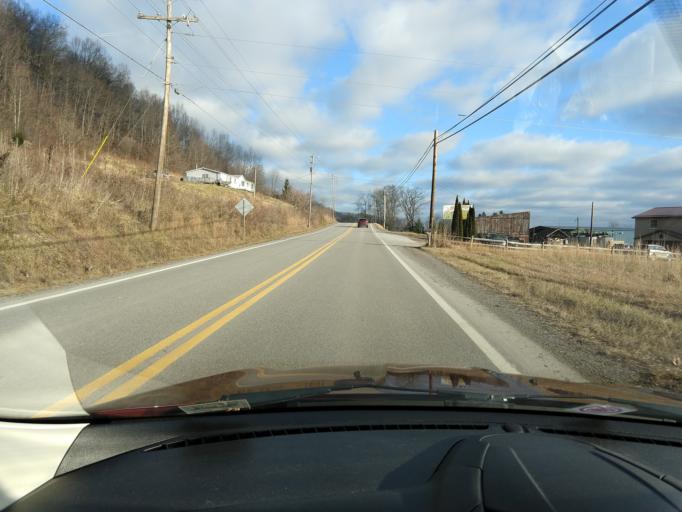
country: US
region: West Virginia
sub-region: Randolph County
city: Elkins
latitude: 38.7390
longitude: -79.9661
